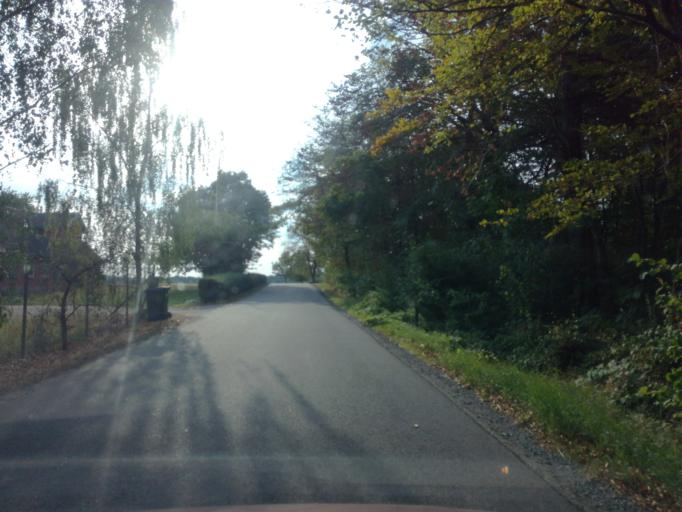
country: DK
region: South Denmark
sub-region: Vejle Kommune
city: Vejle
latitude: 55.6473
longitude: 9.5527
